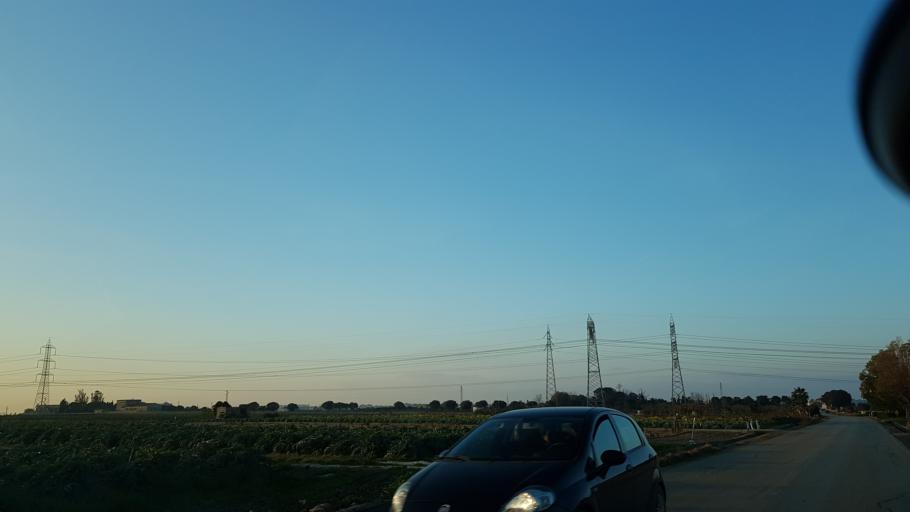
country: IT
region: Apulia
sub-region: Provincia di Brindisi
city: La Rosa
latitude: 40.5988
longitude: 17.9466
